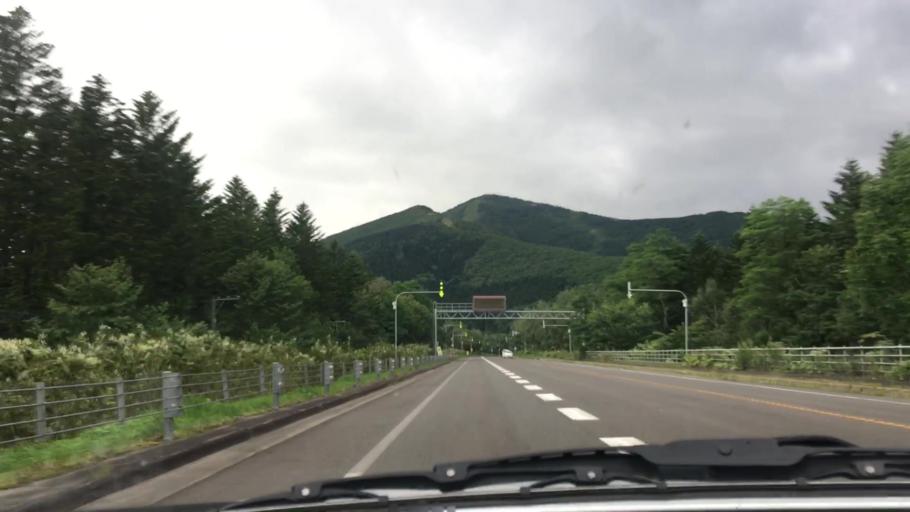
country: JP
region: Hokkaido
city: Otofuke
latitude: 43.1615
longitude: 142.8150
